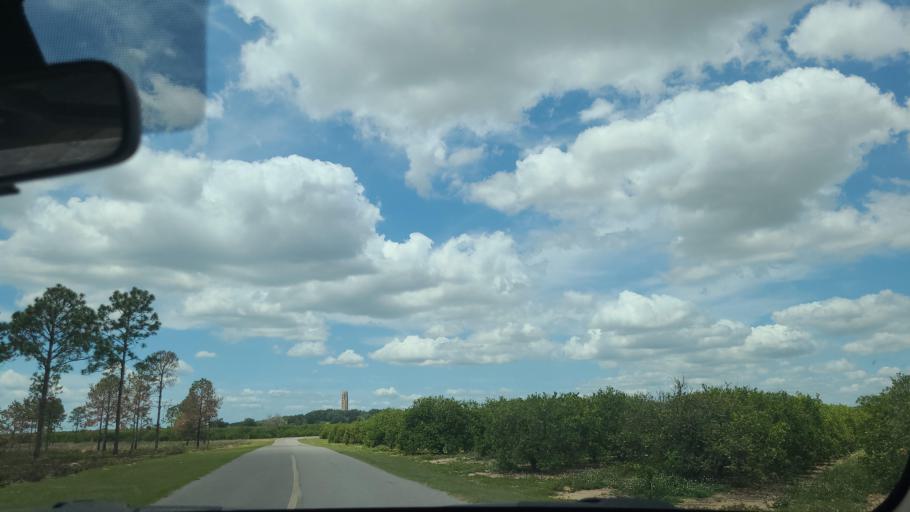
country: US
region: Florida
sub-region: Polk County
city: Lake Wales
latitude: 27.9252
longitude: -81.5678
